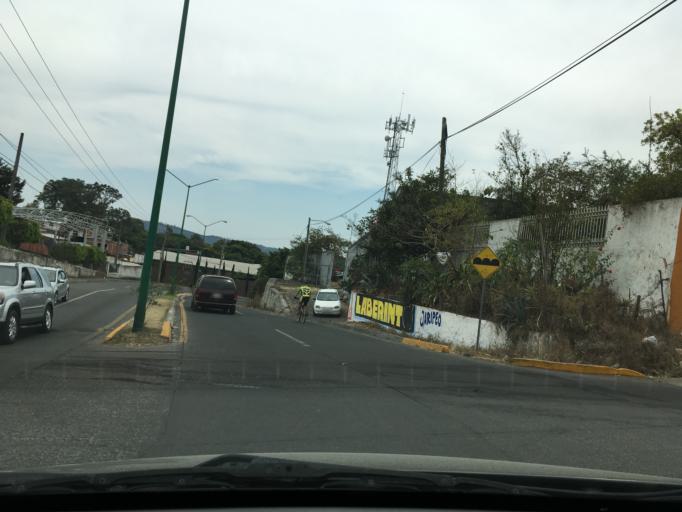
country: MX
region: Michoacan
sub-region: Uruapan
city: Uruapan
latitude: 19.4006
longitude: -102.0683
